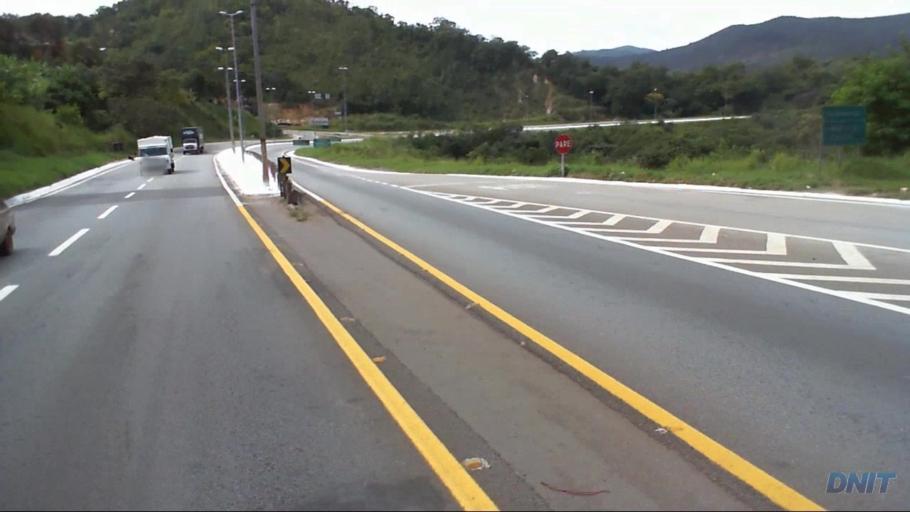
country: BR
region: Minas Gerais
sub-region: Santa Luzia
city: Santa Luzia
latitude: -19.7991
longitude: -43.7565
